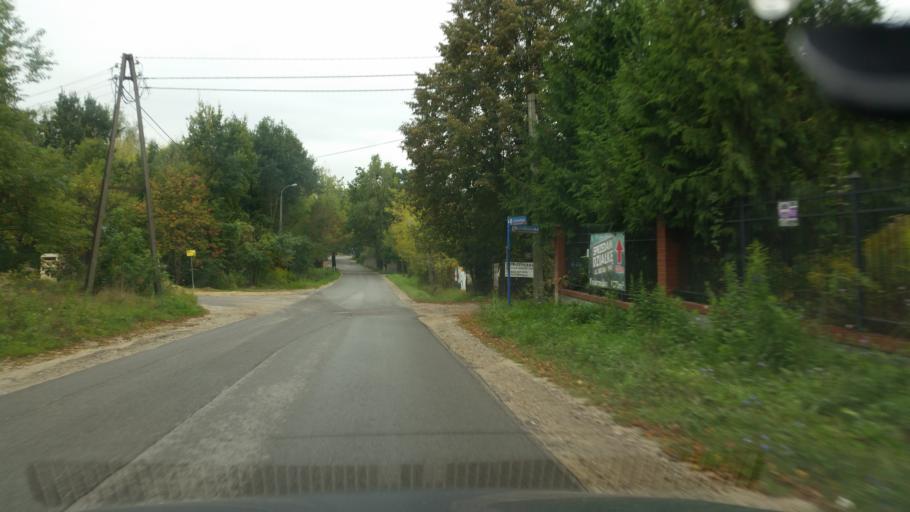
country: PL
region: Masovian Voivodeship
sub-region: Powiat piaseczynski
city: Jozefoslaw
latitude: 52.0923
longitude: 21.0763
